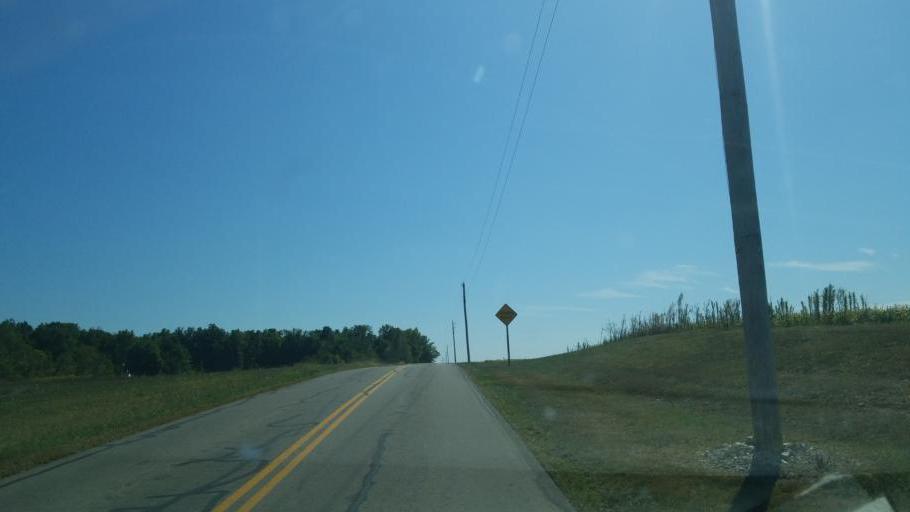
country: US
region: Ohio
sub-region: Logan County
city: Bellefontaine
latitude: 40.3968
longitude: -83.7696
